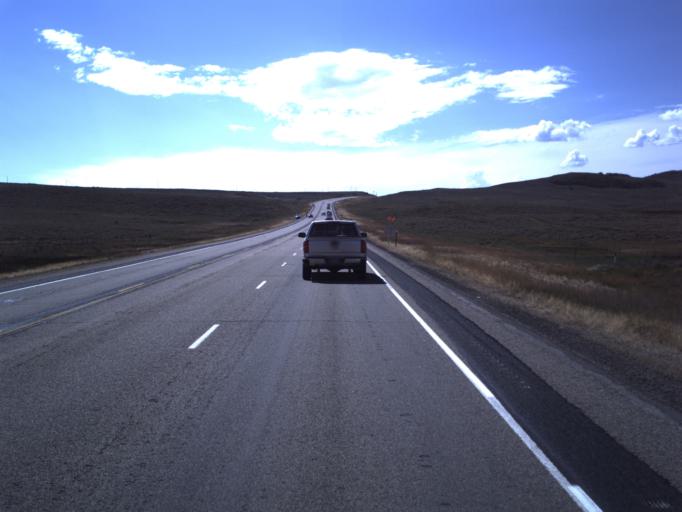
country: US
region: Utah
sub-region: Summit County
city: Francis
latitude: 40.1822
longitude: -111.0394
